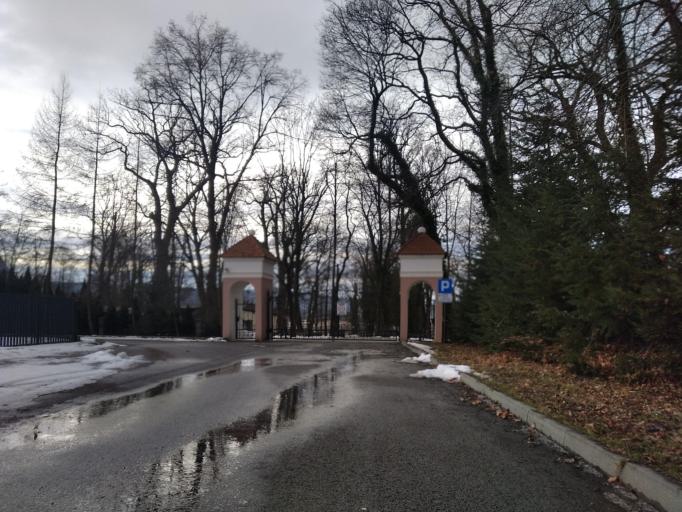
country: PL
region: Subcarpathian Voivodeship
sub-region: Powiat przemyski
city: Dubiecko
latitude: 49.8224
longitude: 22.3956
